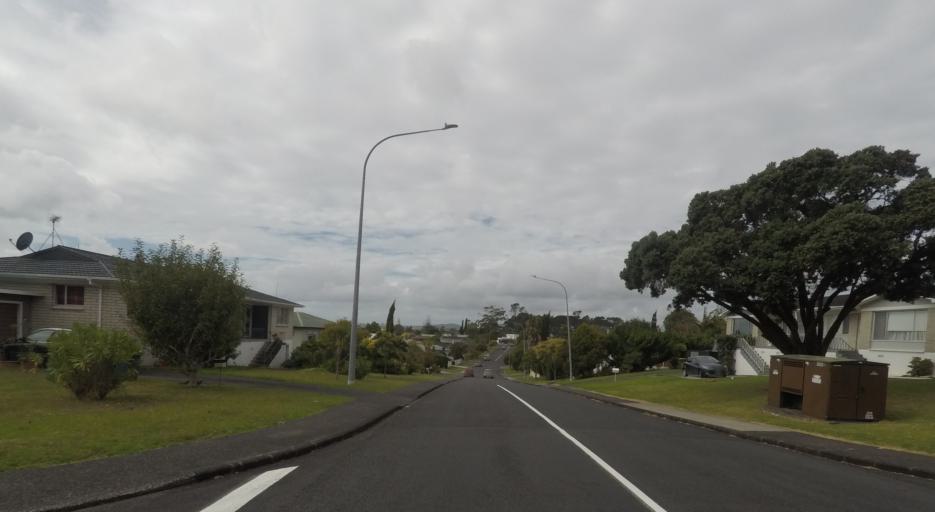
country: NZ
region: Auckland
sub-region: Auckland
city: Rosebank
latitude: -36.8895
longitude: 174.6460
